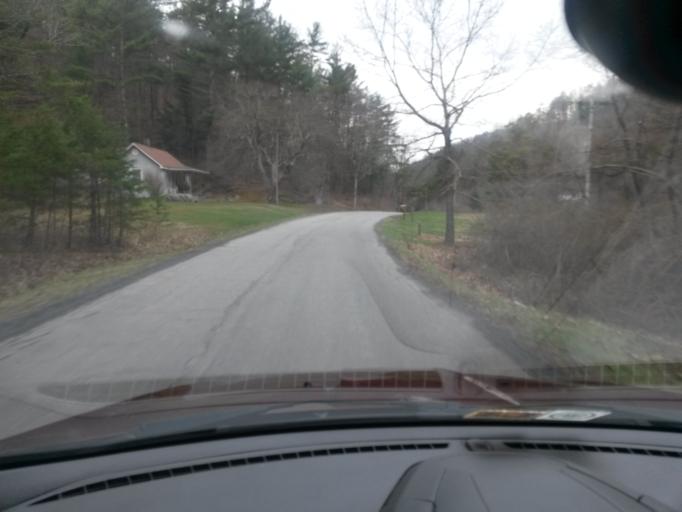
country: US
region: Virginia
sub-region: Bath County
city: Warm Springs
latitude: 38.0150
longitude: -79.8714
